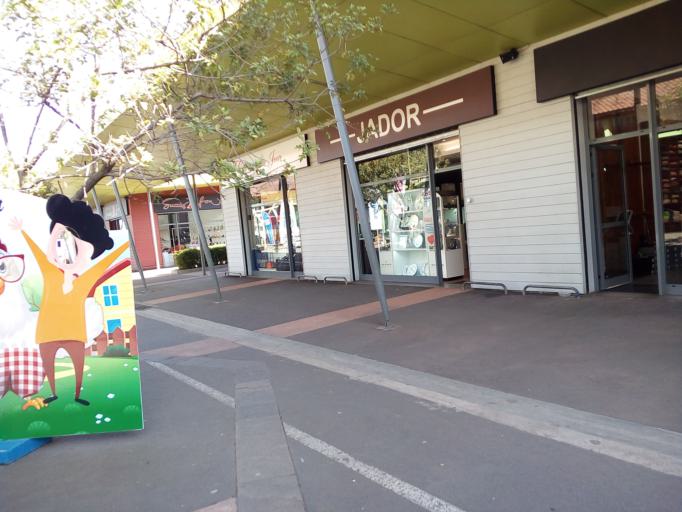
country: MG
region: Analamanga
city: Antananarivo
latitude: -18.8838
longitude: 47.5259
